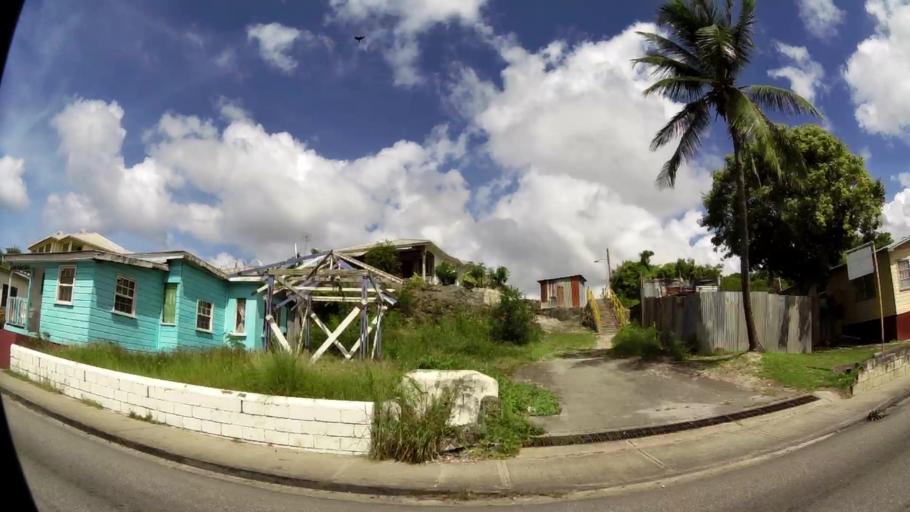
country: BB
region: Saint Michael
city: Bridgetown
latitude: 13.1296
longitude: -59.6313
